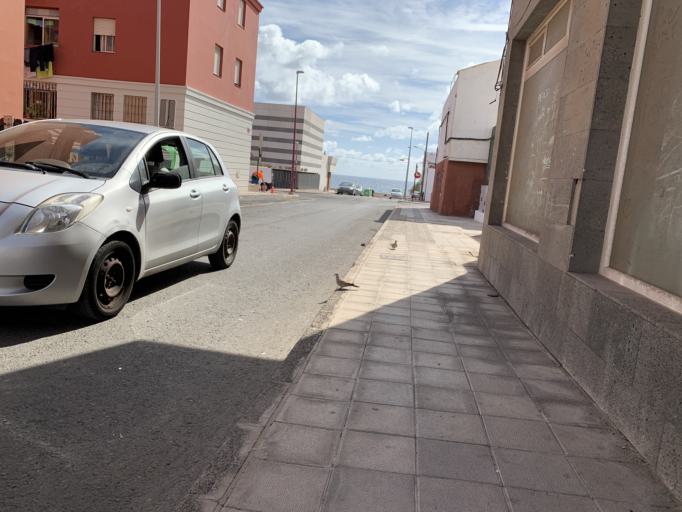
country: ES
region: Canary Islands
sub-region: Provincia de Las Palmas
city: Puerto del Rosario
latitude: 28.5024
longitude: -13.8486
